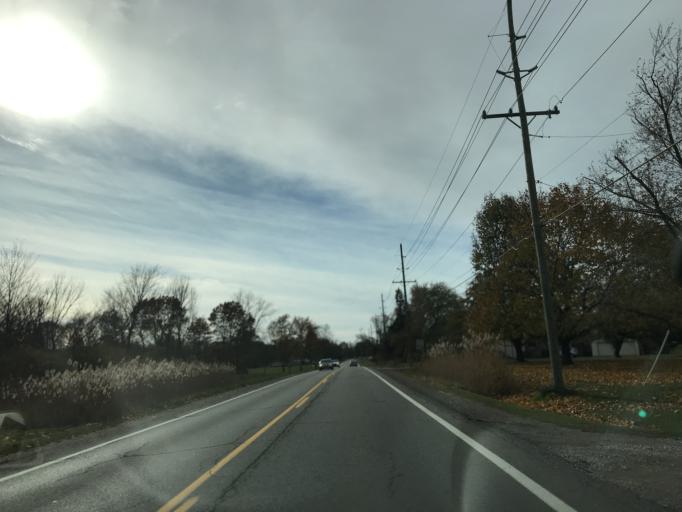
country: US
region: Michigan
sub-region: Oakland County
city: South Lyon
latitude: 42.5078
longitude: -83.6236
